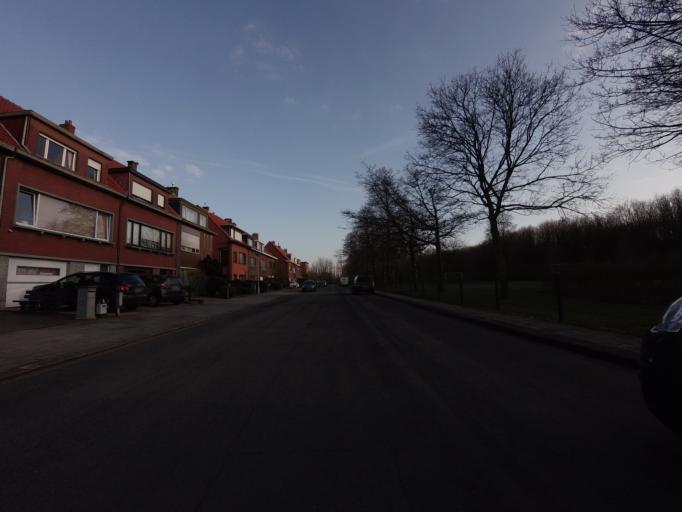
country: BE
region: Flanders
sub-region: Provincie Antwerpen
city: Kapellen
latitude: 51.2723
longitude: 4.4075
